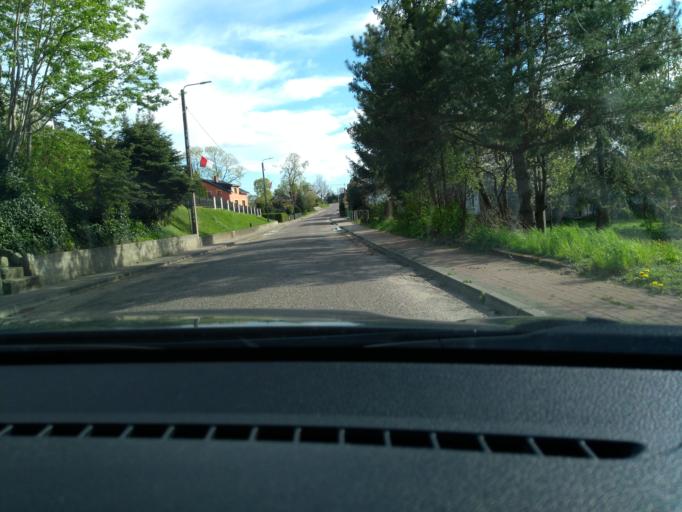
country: PL
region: Pomeranian Voivodeship
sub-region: Powiat leborski
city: Cewice
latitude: 54.3384
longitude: 17.6853
